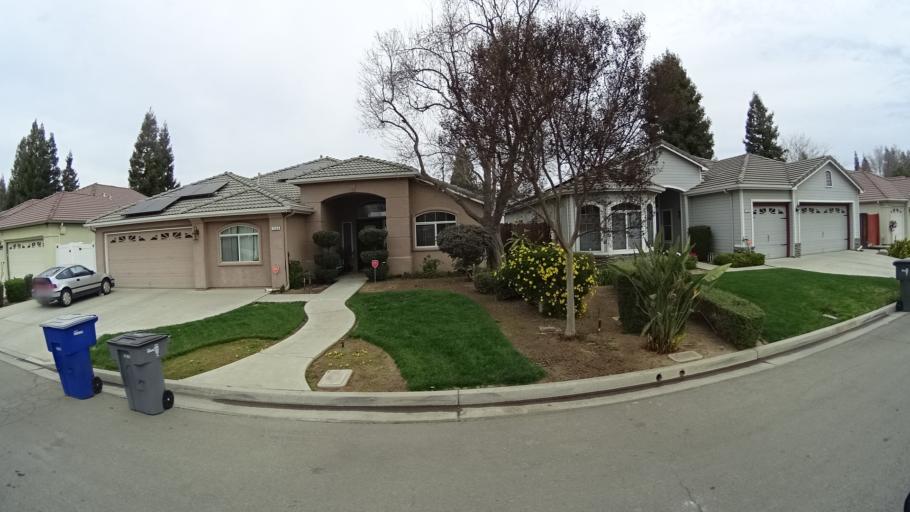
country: US
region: California
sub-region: Fresno County
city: Clovis
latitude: 36.8554
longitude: -119.7410
